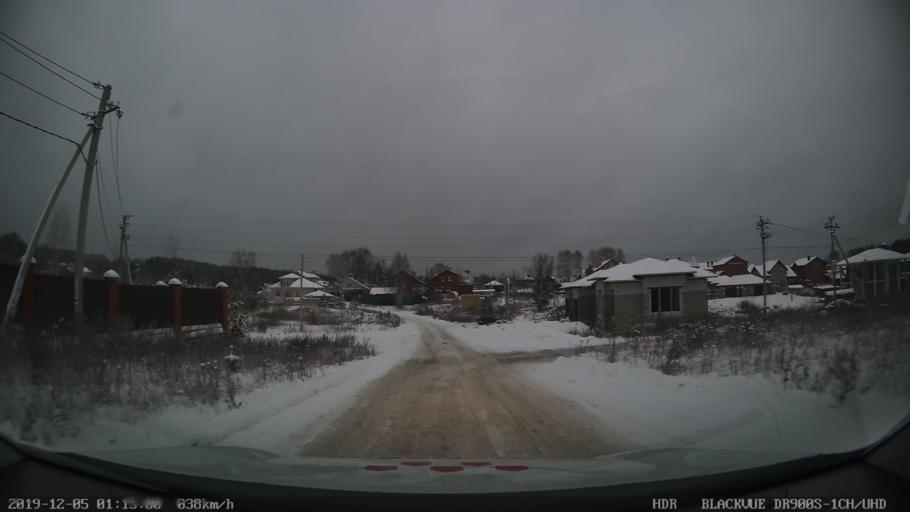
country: RU
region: Tatarstan
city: Stolbishchi
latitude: 55.6445
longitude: 49.1141
